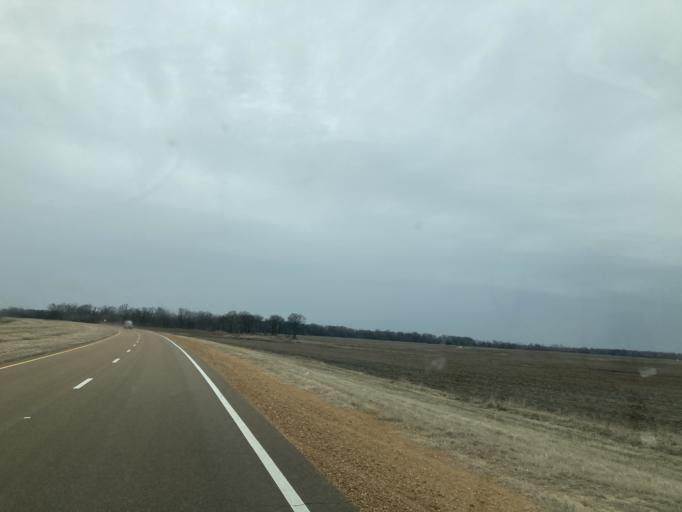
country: US
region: Mississippi
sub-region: Humphreys County
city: Belzoni
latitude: 33.0709
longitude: -90.4740
